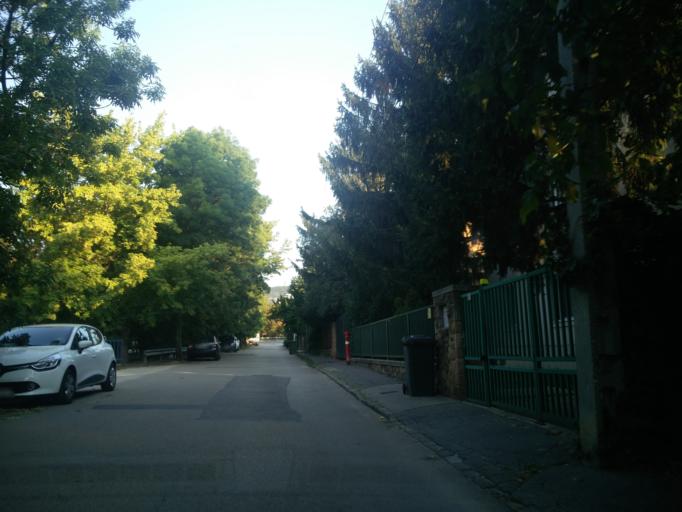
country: HU
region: Budapest
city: Budapest XII. keruelet
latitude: 47.4725
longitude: 19.0046
